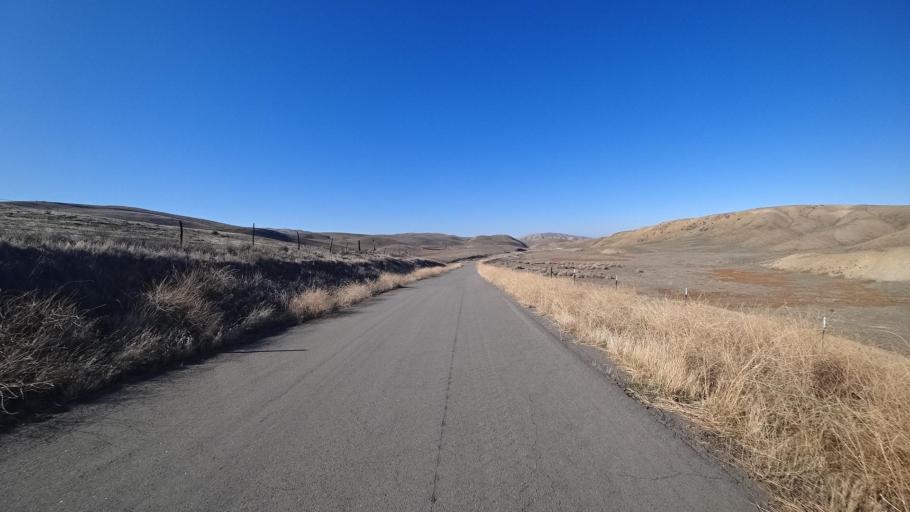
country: US
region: California
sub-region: Kern County
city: Maricopa
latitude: 34.9678
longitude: -119.4510
